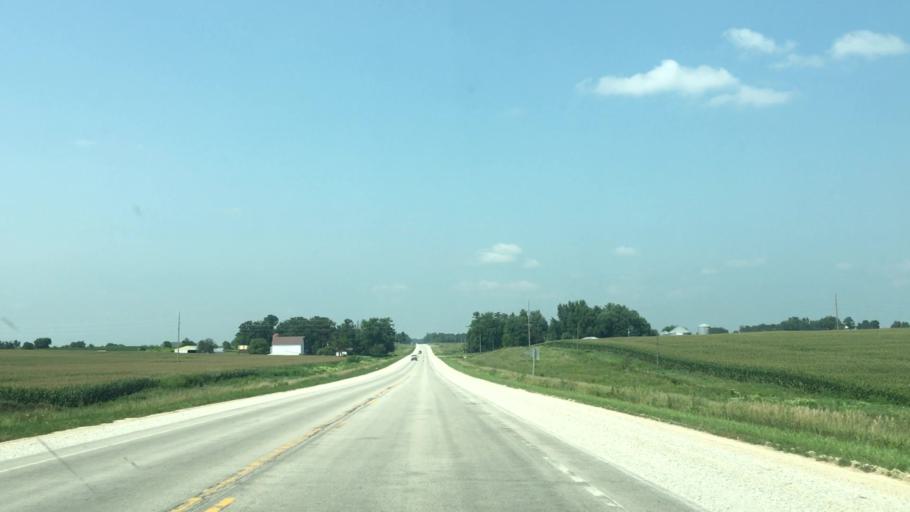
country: US
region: Minnesota
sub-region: Fillmore County
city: Harmony
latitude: 43.4766
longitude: -91.8702
